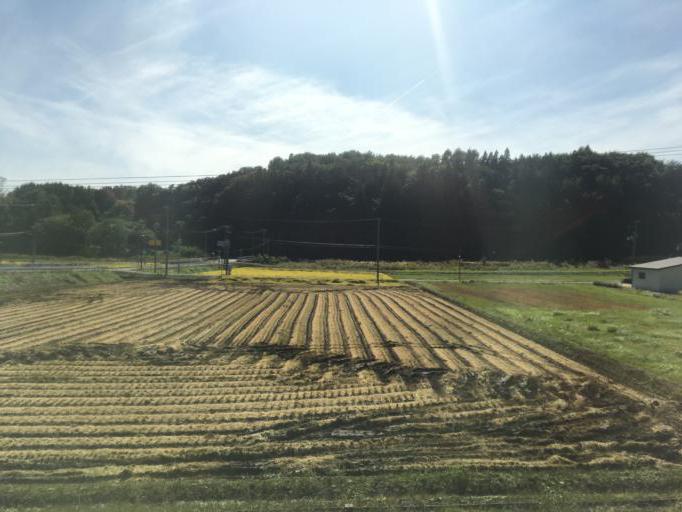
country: JP
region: Iwate
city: Shizukuishi
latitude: 39.9688
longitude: 141.0456
